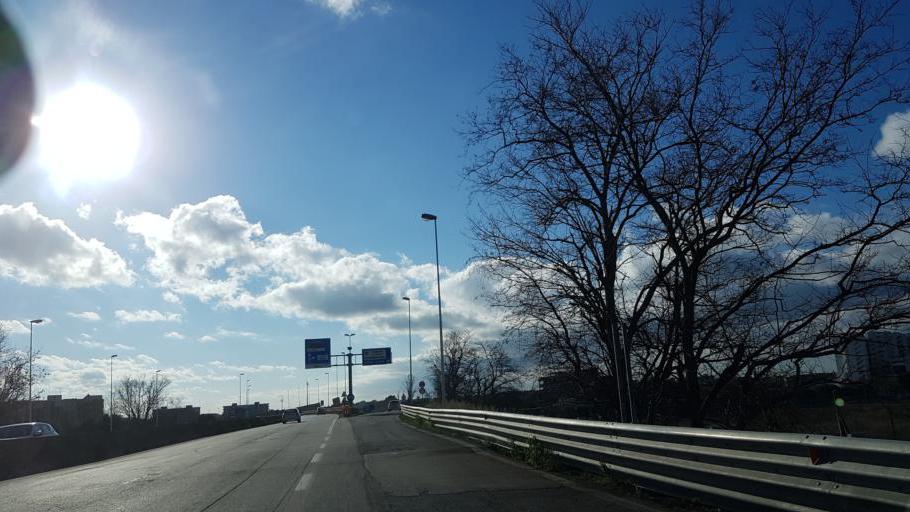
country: IT
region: Apulia
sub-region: Provincia di Brindisi
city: Brindisi
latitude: 40.6296
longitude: 17.9182
